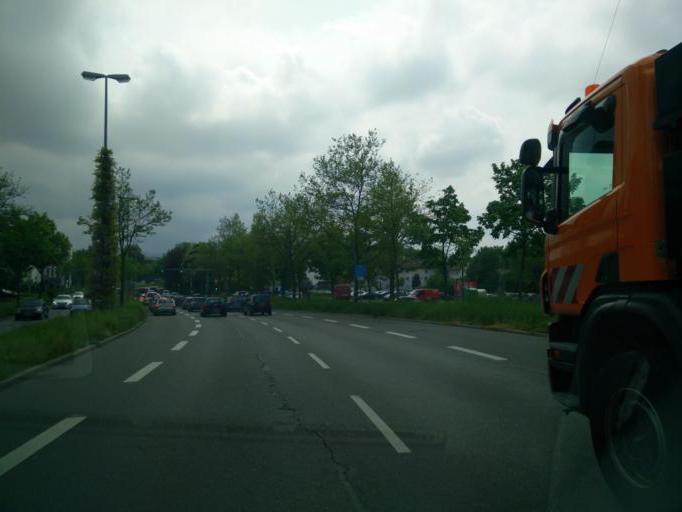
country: DE
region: Baden-Wuerttemberg
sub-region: Tuebingen Region
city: Reutlingen
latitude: 48.4993
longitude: 9.1976
